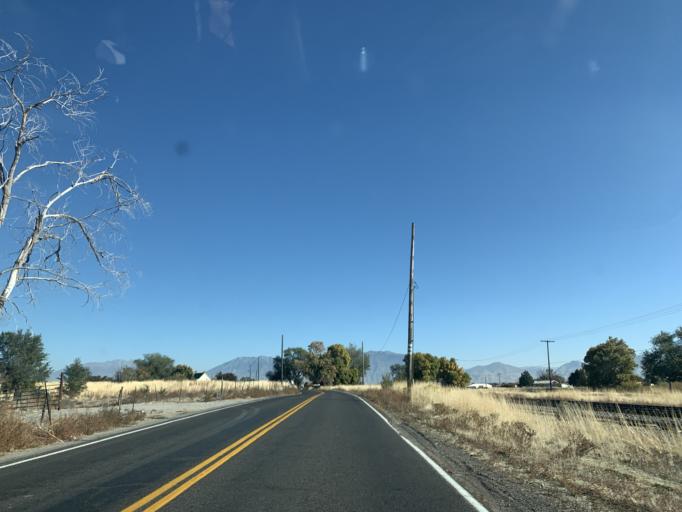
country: US
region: Utah
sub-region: Utah County
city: Payson
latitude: 40.0417
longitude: -111.7612
